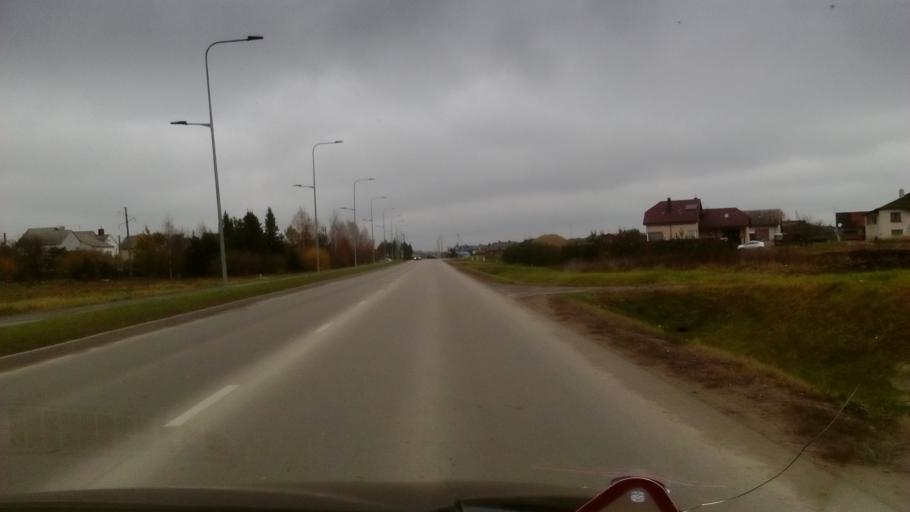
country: LT
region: Marijampoles apskritis
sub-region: Marijampole Municipality
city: Marijampole
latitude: 54.5377
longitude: 23.3667
